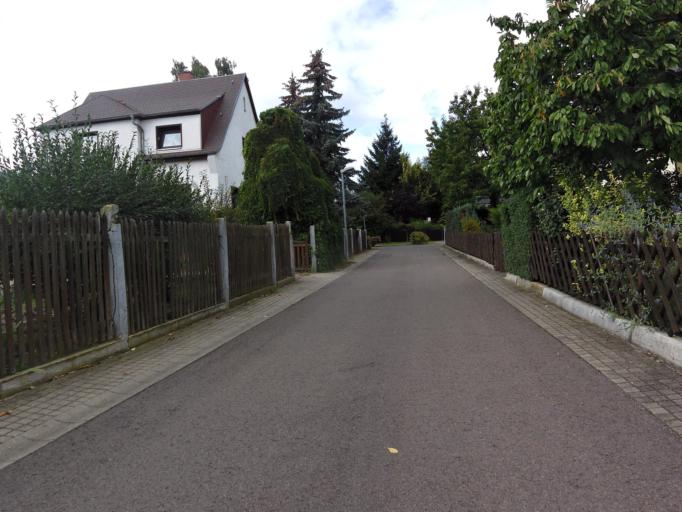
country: DE
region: Saxony
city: Leipzig
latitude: 51.3857
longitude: 12.3638
